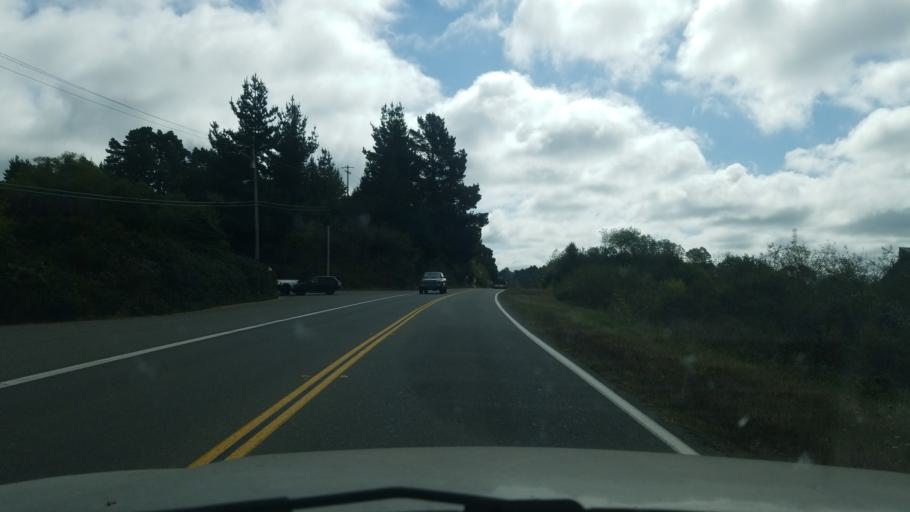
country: US
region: California
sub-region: Humboldt County
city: Fortuna
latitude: 40.6189
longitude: -124.2069
